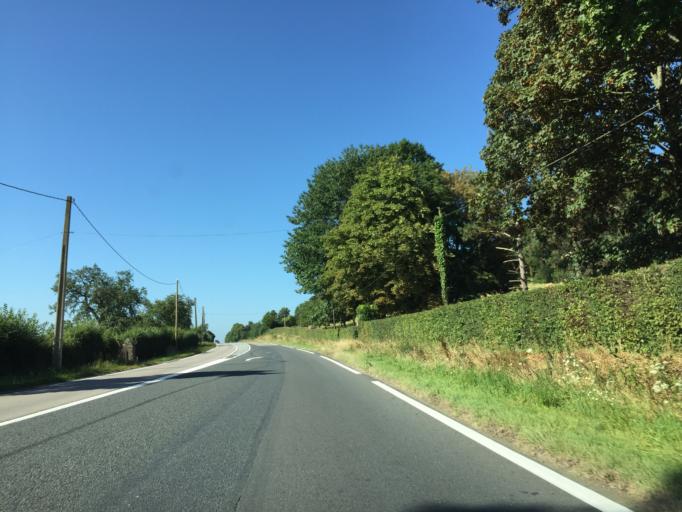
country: FR
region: Lower Normandy
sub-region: Departement du Calvados
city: Lisieux
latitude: 49.1682
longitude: 0.2277
